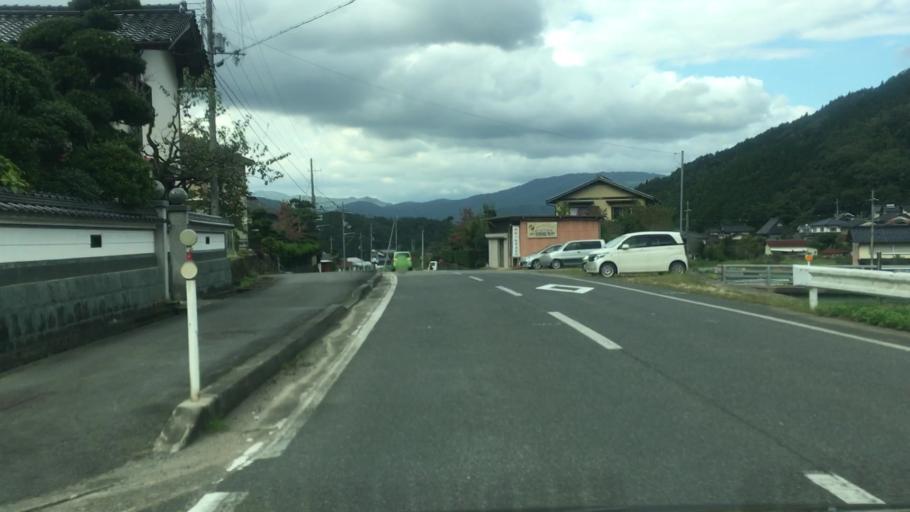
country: JP
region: Hyogo
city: Toyooka
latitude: 35.4372
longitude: 134.7341
